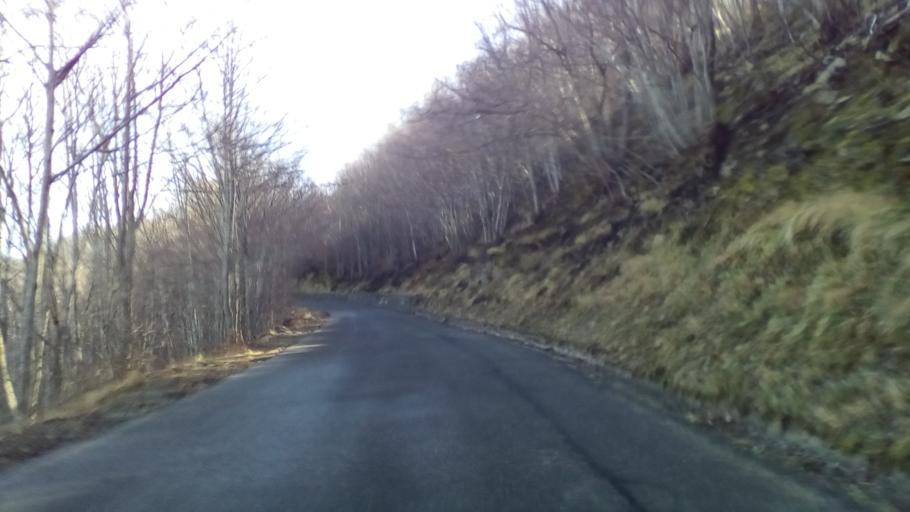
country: IT
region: Tuscany
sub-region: Provincia di Lucca
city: Castiglione di Garfagnana
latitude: 44.1653
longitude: 10.4462
